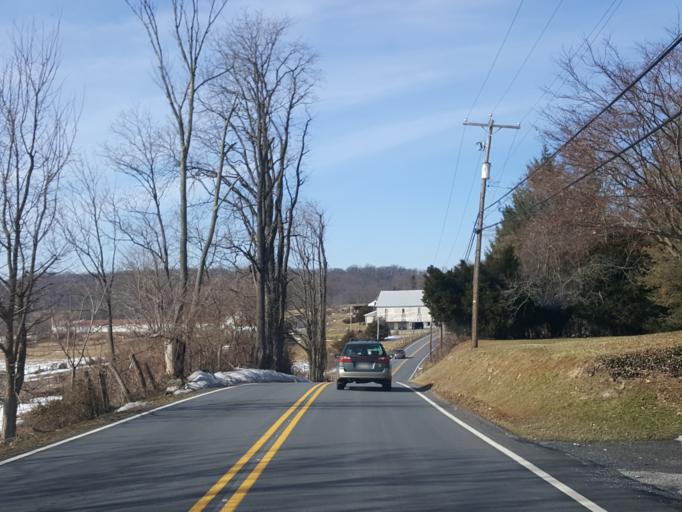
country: US
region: Pennsylvania
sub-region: Lebanon County
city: Campbelltown
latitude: 40.2525
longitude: -76.5469
